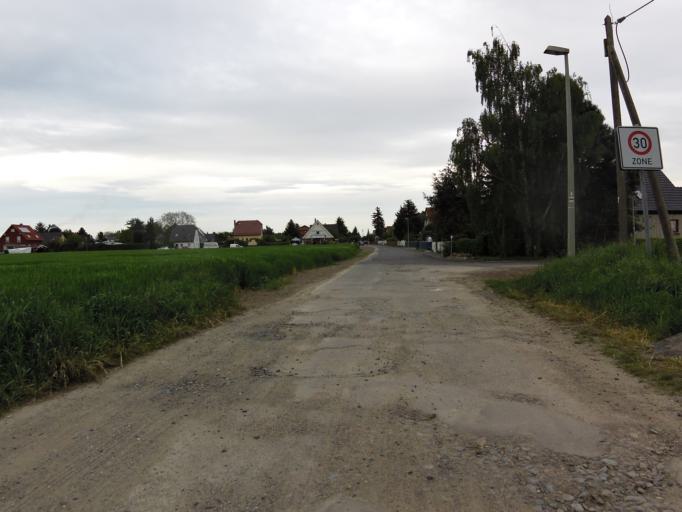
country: DE
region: Saxony
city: Zwenkau
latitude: 51.2782
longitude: 12.2924
